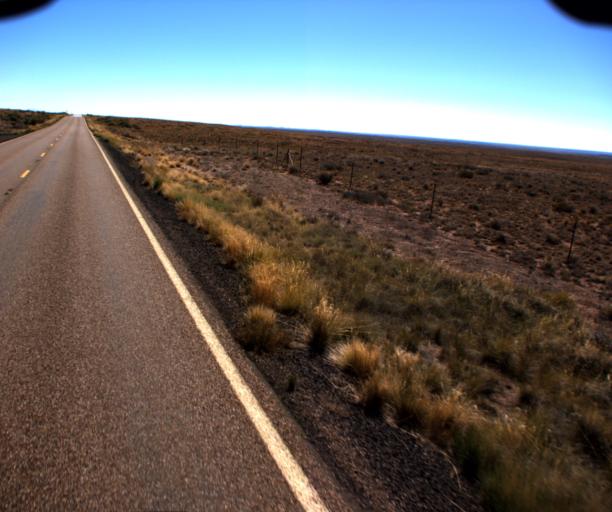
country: US
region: Arizona
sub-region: Navajo County
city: Holbrook
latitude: 35.0134
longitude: -110.0900
